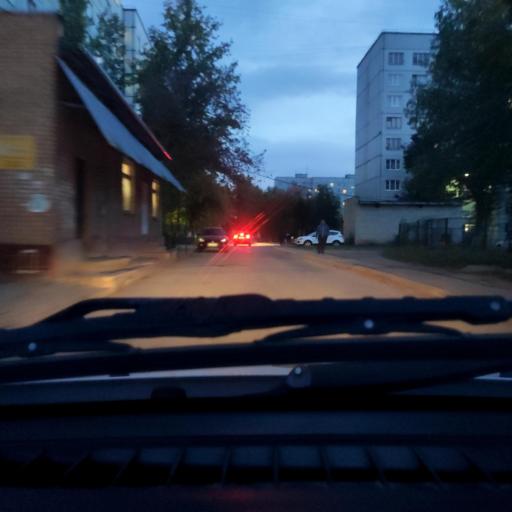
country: RU
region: Samara
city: Zhigulevsk
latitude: 53.4738
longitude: 49.5160
